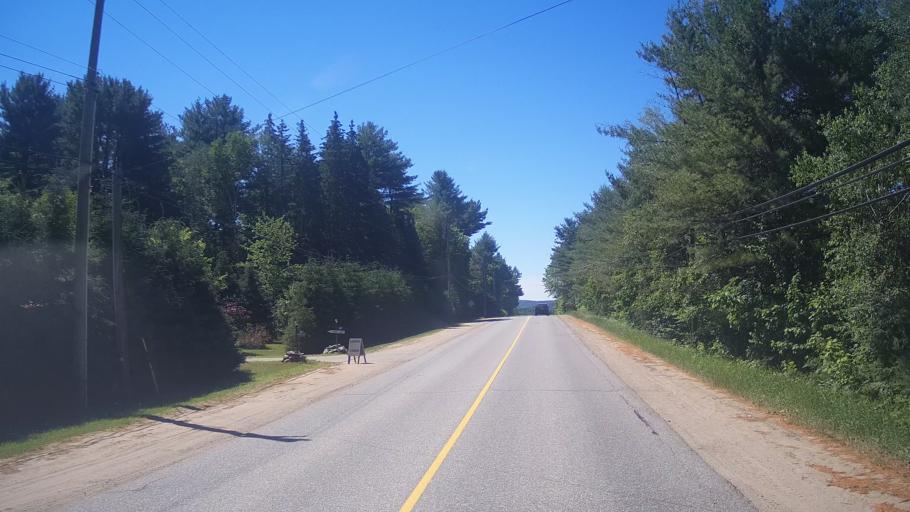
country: CA
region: Ontario
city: Huntsville
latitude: 45.3579
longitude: -79.2035
